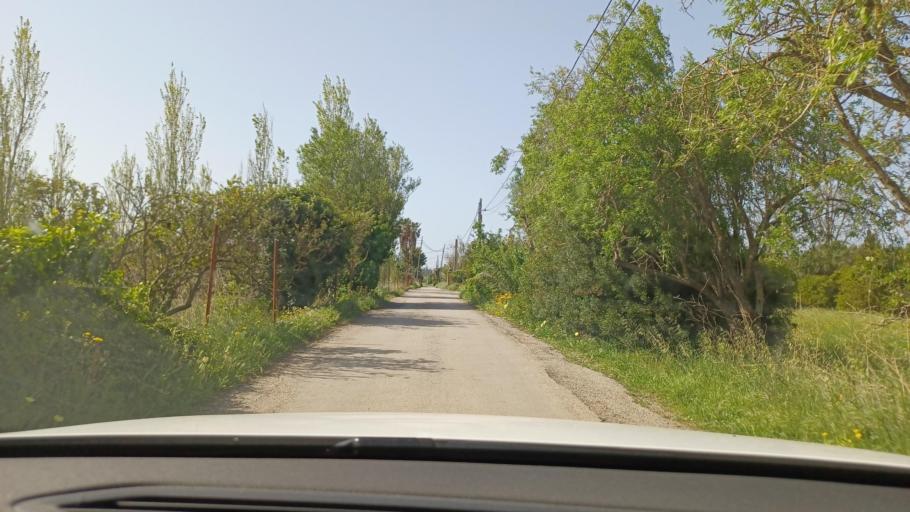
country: ES
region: Catalonia
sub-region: Provincia de Tarragona
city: Tortosa
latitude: 40.7937
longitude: 0.5152
